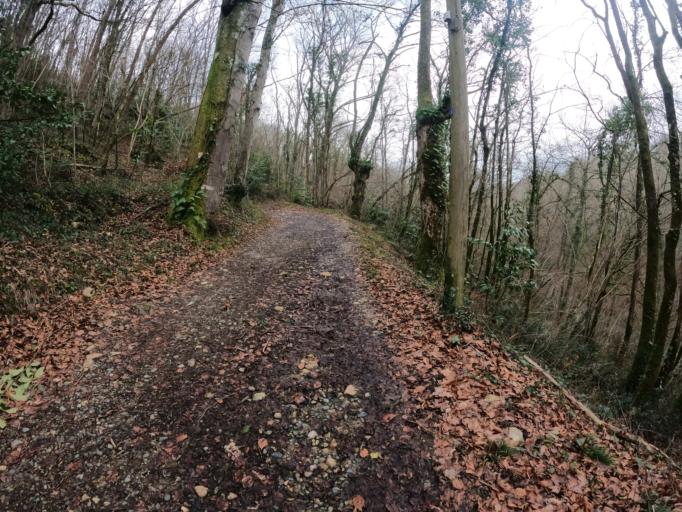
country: FR
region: Aquitaine
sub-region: Departement des Pyrenees-Atlantiques
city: Mazeres-Lezons
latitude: 43.2725
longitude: -0.3590
